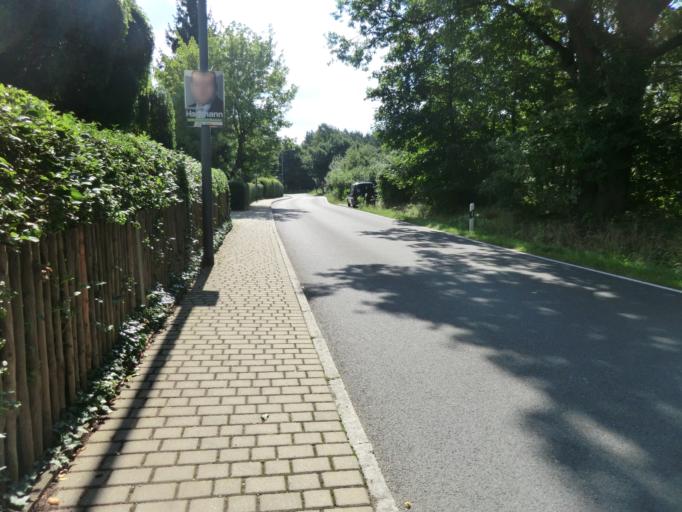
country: DE
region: Saxony
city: Albertstadt
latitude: 51.1066
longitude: 13.7608
